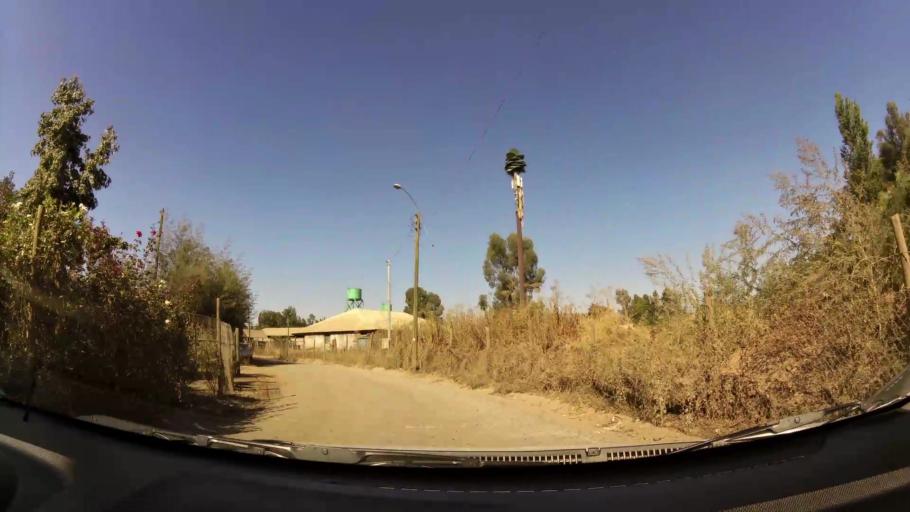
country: CL
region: Maule
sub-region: Provincia de Talca
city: Talca
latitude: -35.4223
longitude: -71.6060
